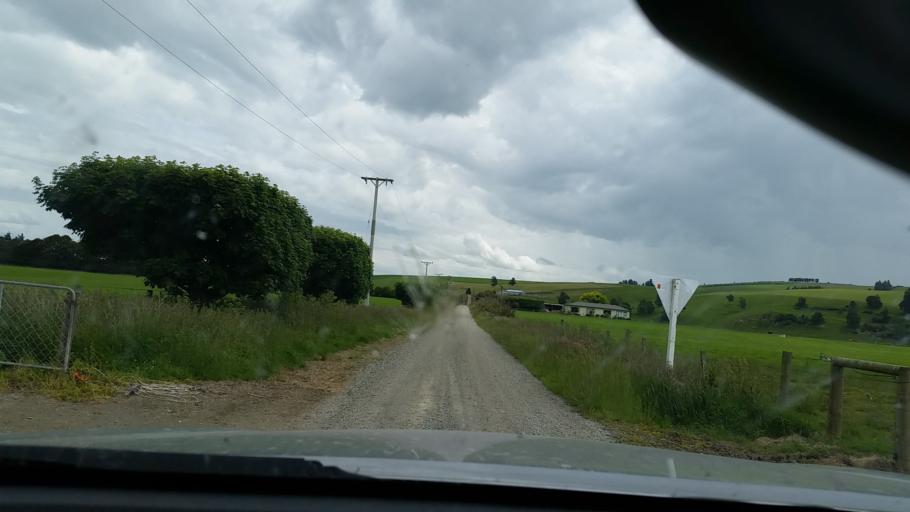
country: NZ
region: Southland
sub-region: Southland District
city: Winton
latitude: -46.0215
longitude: 168.3112
